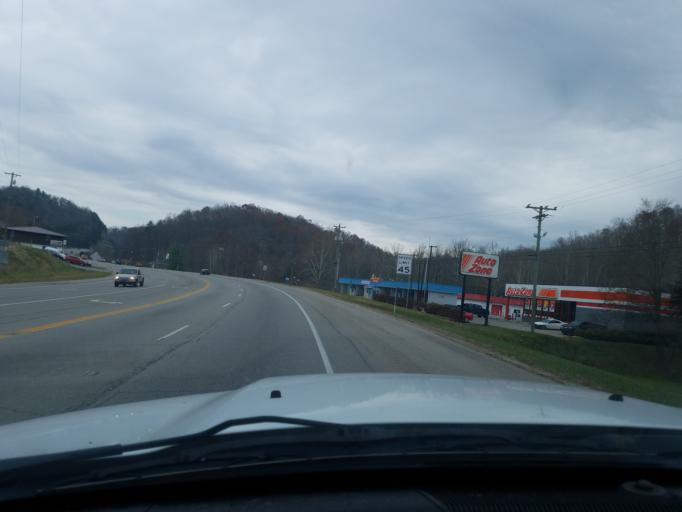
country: US
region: Kentucky
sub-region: Rowan County
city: Morehead
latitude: 38.1871
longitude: -83.4763
